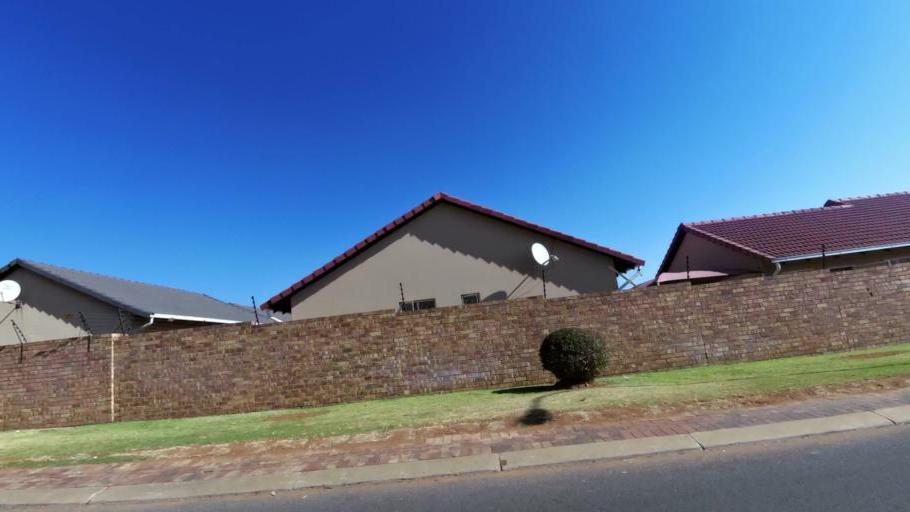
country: ZA
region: Gauteng
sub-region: City of Johannesburg Metropolitan Municipality
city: Johannesburg
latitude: -26.2419
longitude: 27.9998
